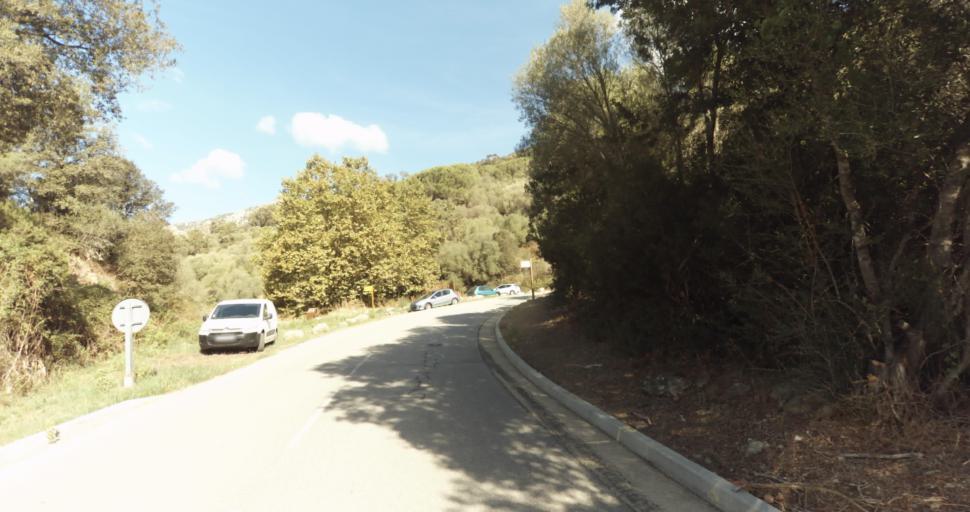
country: FR
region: Corsica
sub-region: Departement de la Corse-du-Sud
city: Ajaccio
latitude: 41.9310
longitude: 8.7020
